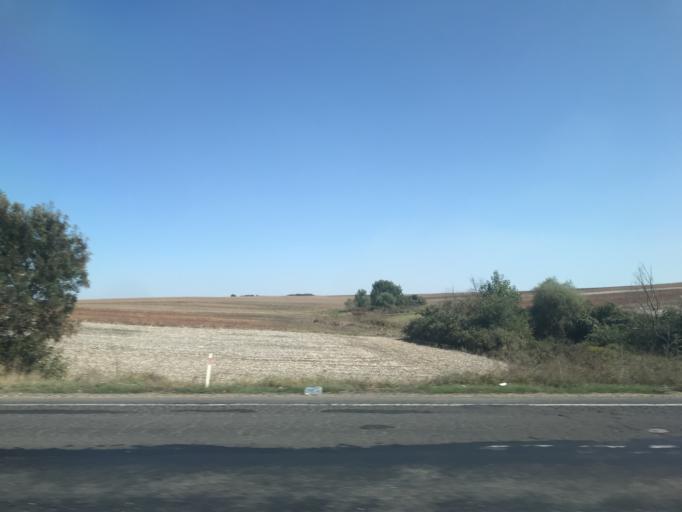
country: TR
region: Tekirdag
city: Muratli
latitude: 41.1115
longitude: 27.4915
